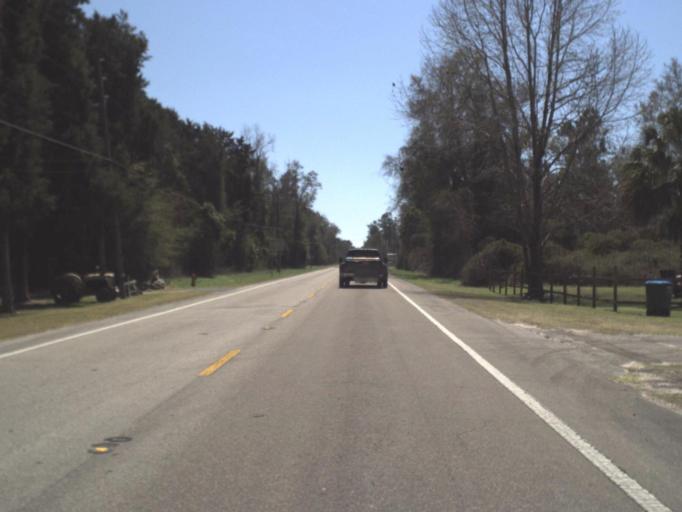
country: US
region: Florida
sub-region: Leon County
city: Woodville
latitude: 30.2483
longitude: -84.2335
